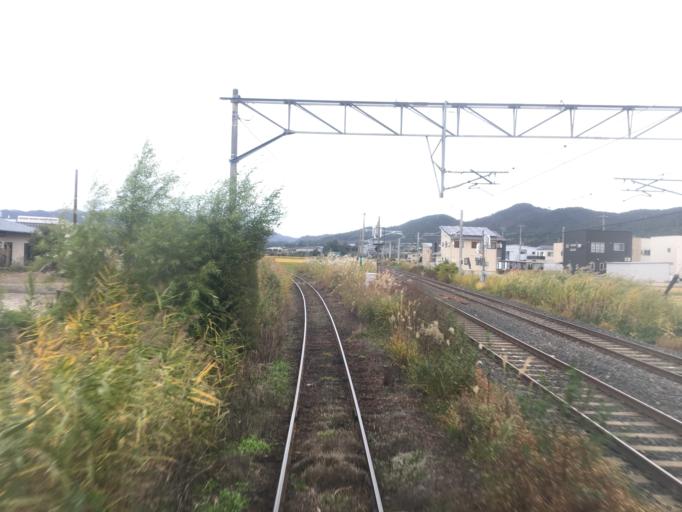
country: JP
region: Yamagata
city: Takahata
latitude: 38.0563
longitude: 140.1485
